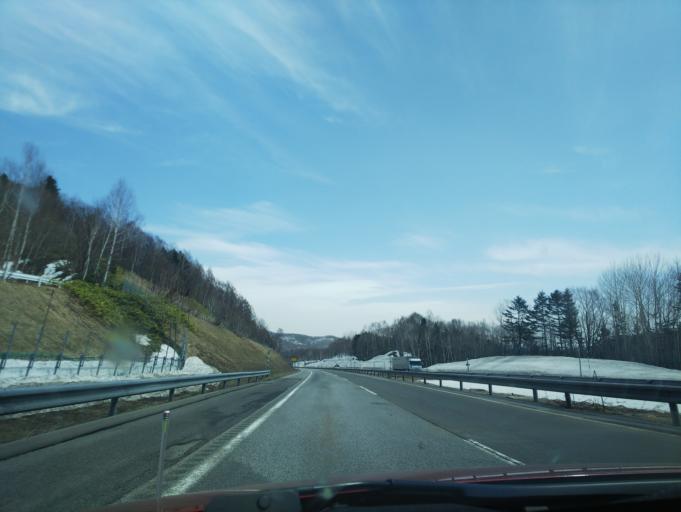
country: JP
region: Hokkaido
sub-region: Asahikawa-shi
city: Asahikawa
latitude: 43.7924
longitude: 142.2691
